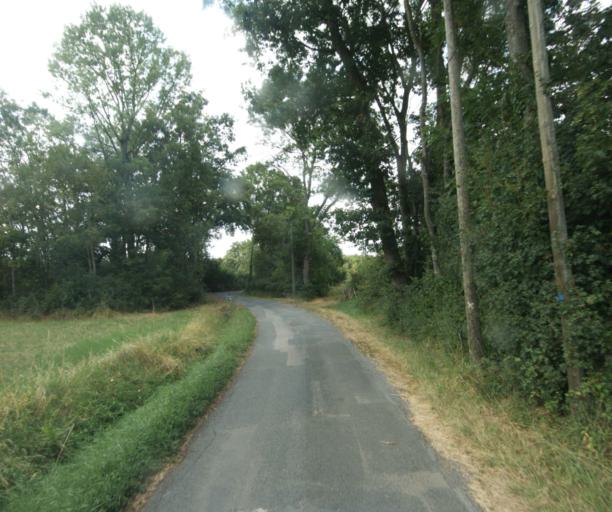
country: FR
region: Rhone-Alpes
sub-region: Departement du Rhone
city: Saint-Germain-Nuelles
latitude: 45.8524
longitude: 4.6022
